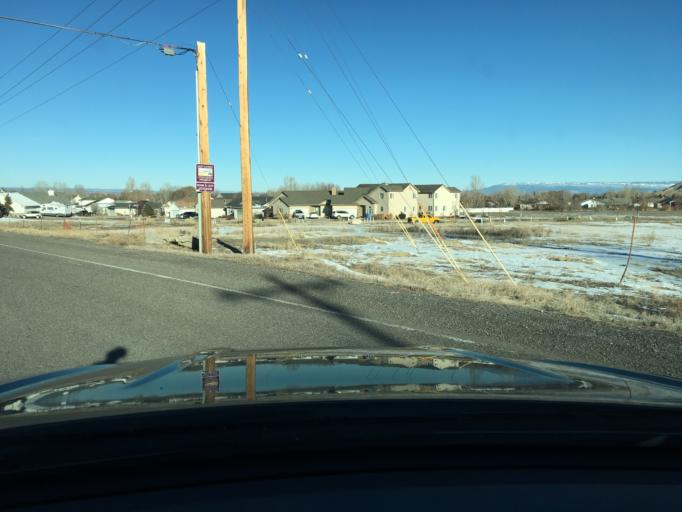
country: US
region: Colorado
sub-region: Montrose County
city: Montrose
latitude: 38.4745
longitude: -107.8387
